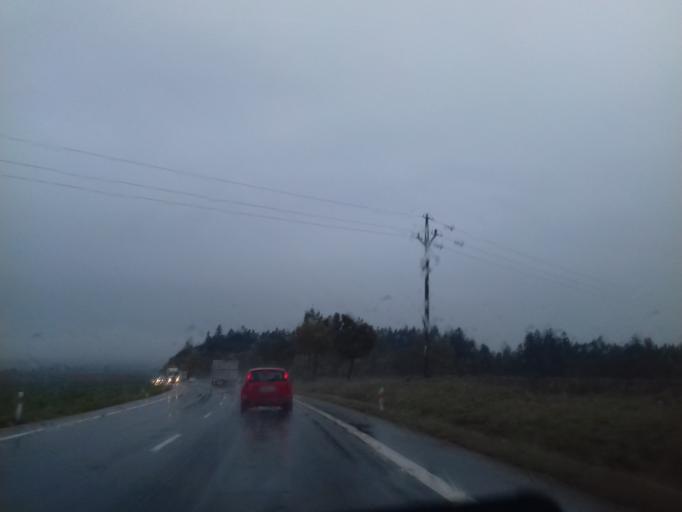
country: CZ
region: Pardubicky
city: Opatov
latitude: 49.7822
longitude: 16.5130
